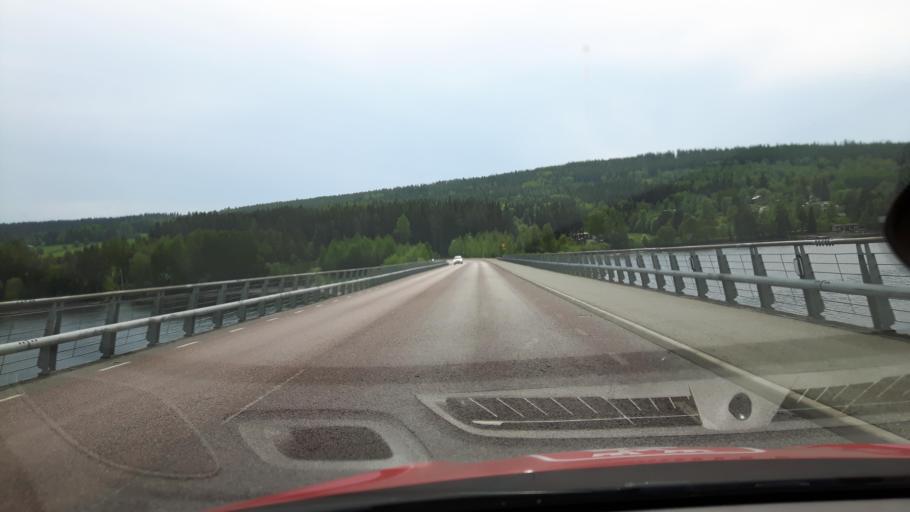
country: SE
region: Jaemtland
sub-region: OEstersunds Kommun
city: Ostersund
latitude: 63.1548
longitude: 14.5934
